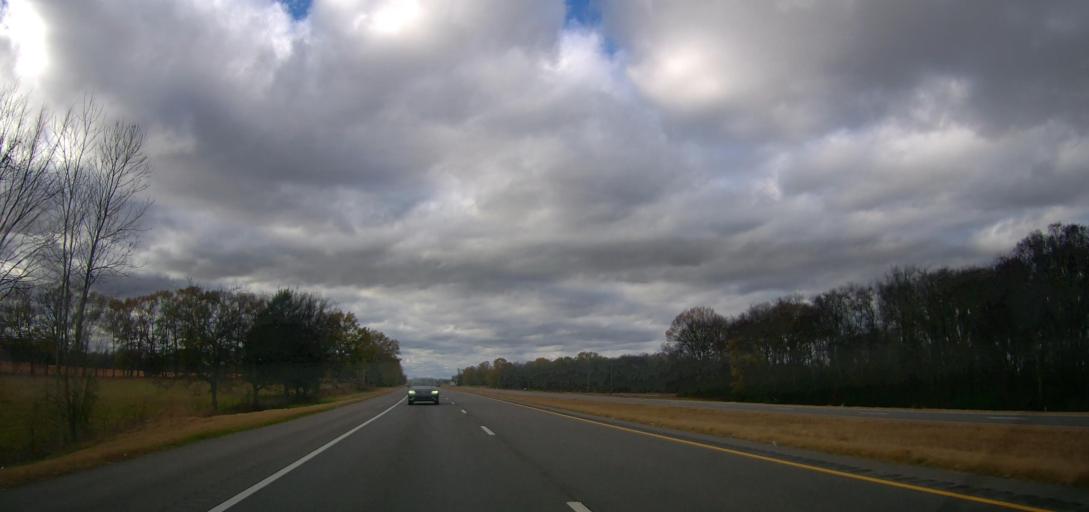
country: US
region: Alabama
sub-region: Lawrence County
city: Moulton
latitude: 34.4579
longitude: -87.2379
